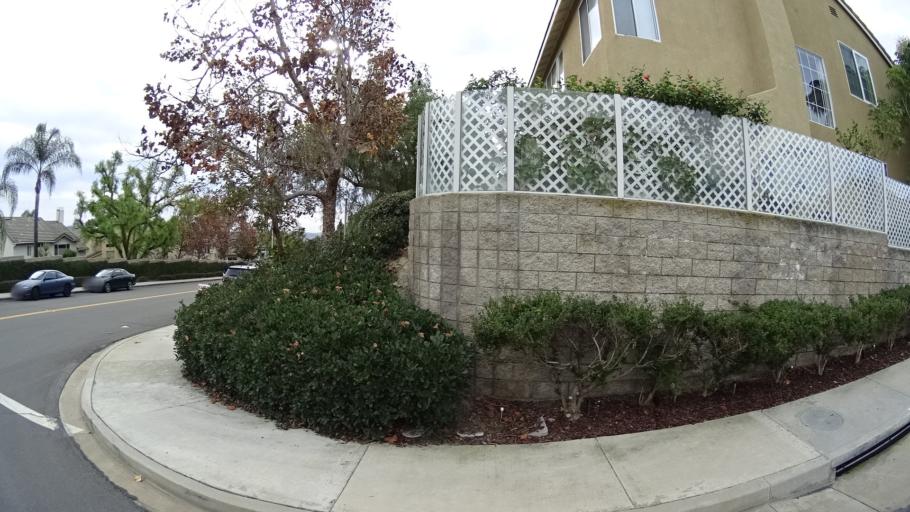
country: US
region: California
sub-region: Orange County
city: Aliso Viejo
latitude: 33.5771
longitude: -117.7379
